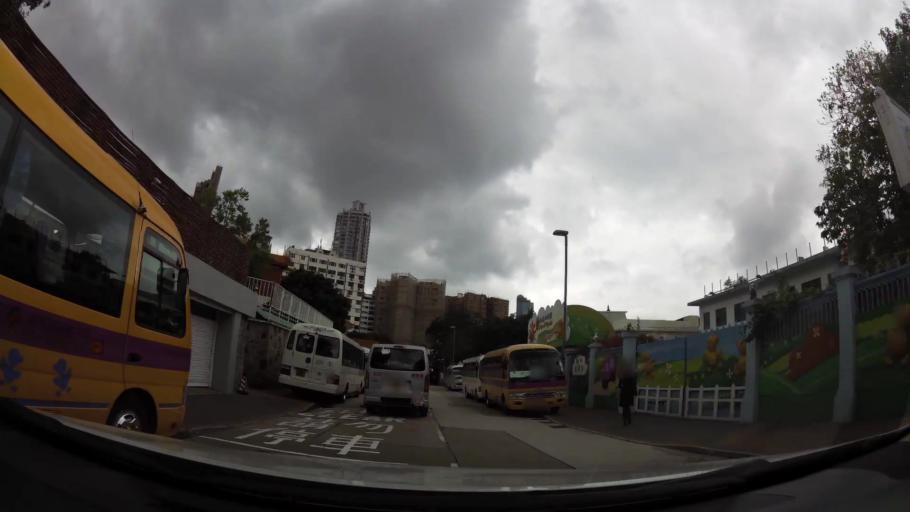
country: HK
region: Kowloon City
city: Kowloon
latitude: 22.3281
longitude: 114.1769
